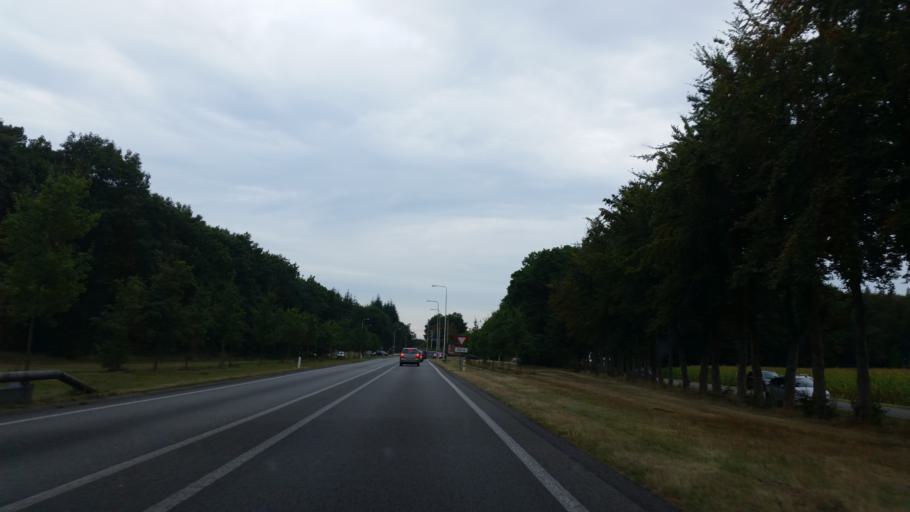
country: NL
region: Gelderland
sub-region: Gemeente Ede
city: Ede
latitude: 52.0674
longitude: 5.6923
